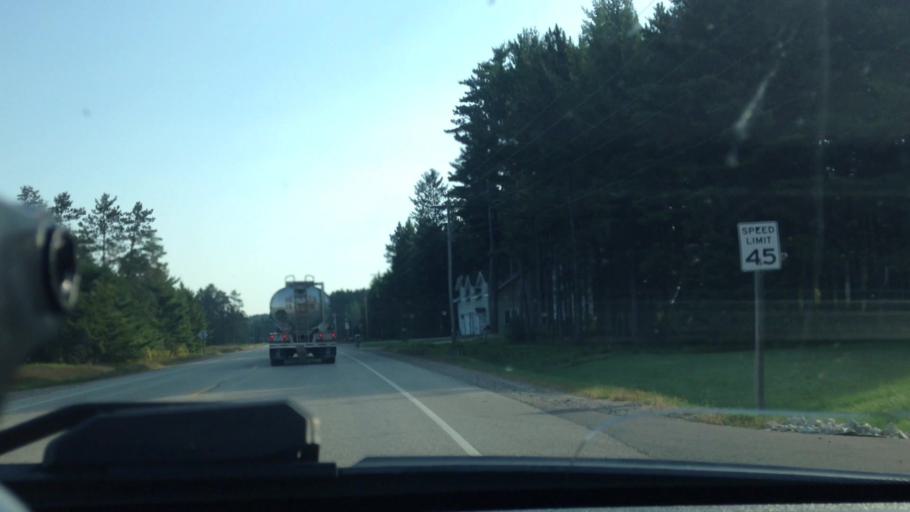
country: US
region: Wisconsin
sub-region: Marinette County
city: Niagara
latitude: 45.6375
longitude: -87.9851
